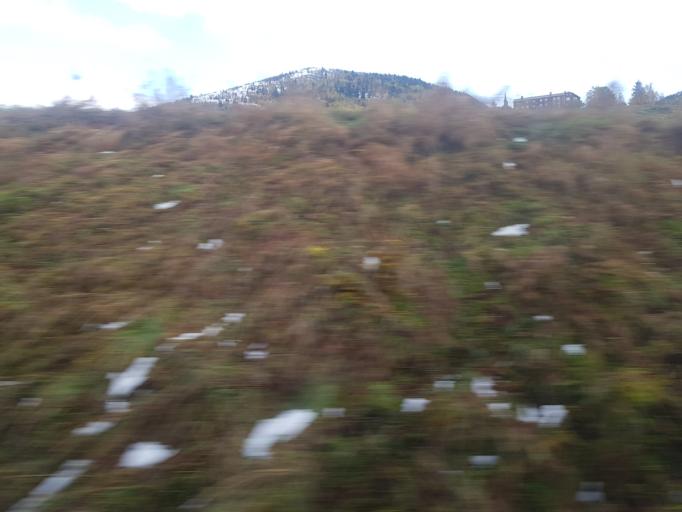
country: NO
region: Oppland
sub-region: Dovre
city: Dovre
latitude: 61.9820
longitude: 9.2444
